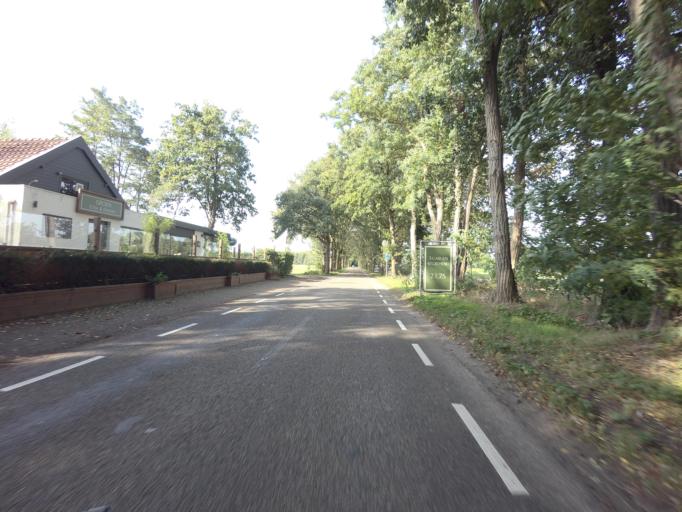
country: NL
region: North Brabant
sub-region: Gemeente Breda
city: Hoge Vucht
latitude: 51.6337
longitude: 4.7944
